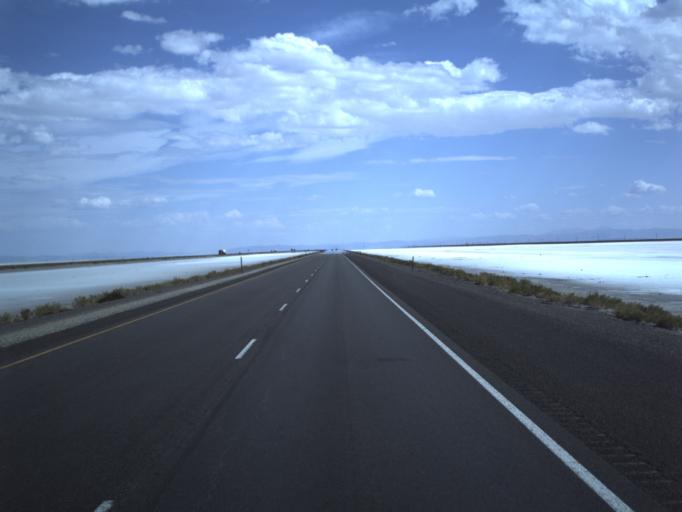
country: US
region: Utah
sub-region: Tooele County
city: Wendover
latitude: 40.7357
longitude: -113.7171
